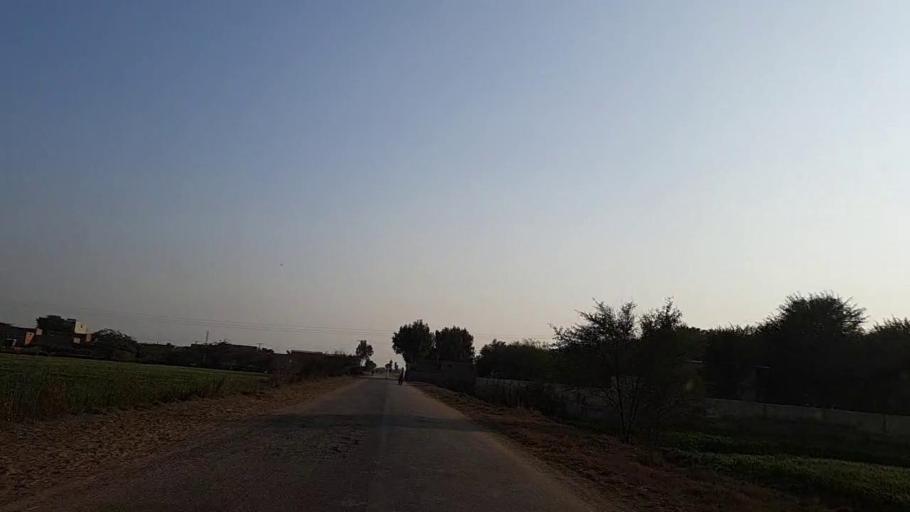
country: PK
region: Sindh
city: Sakrand
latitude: 26.0469
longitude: 68.4214
